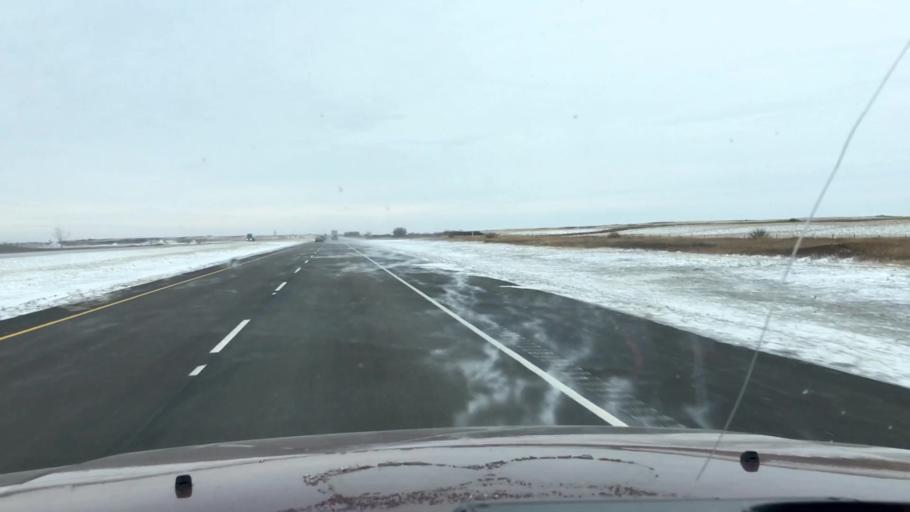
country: CA
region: Saskatchewan
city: Moose Jaw
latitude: 50.8949
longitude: -105.6291
